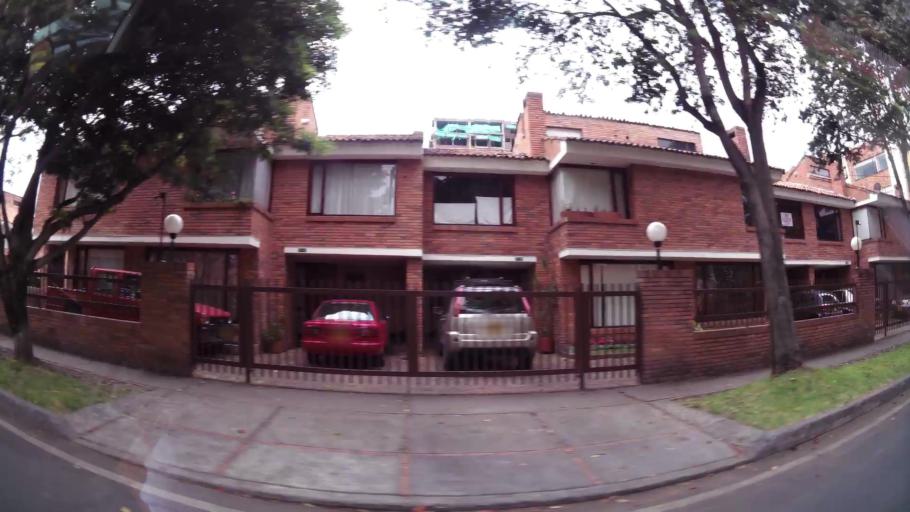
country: CO
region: Bogota D.C.
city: Barrio San Luis
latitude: 4.7226
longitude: -74.0352
